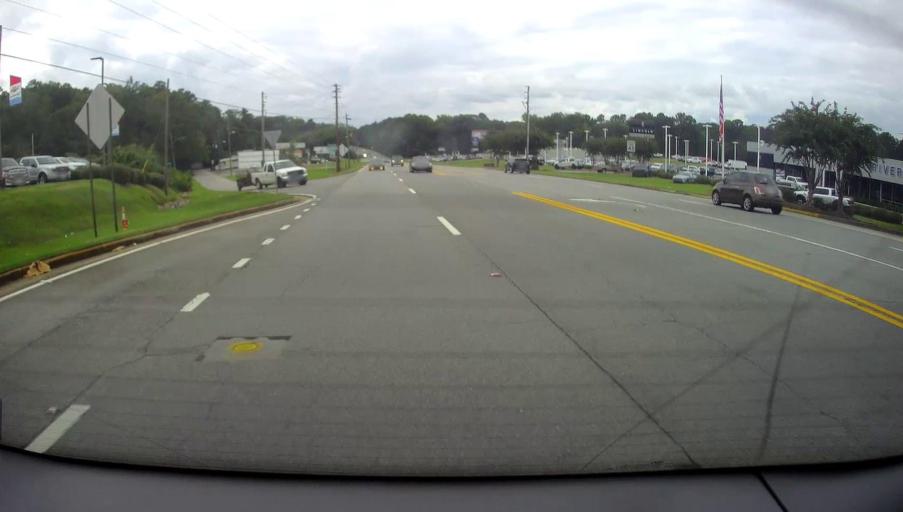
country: US
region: Georgia
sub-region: Bibb County
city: Macon
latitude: 32.8572
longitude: -83.6462
